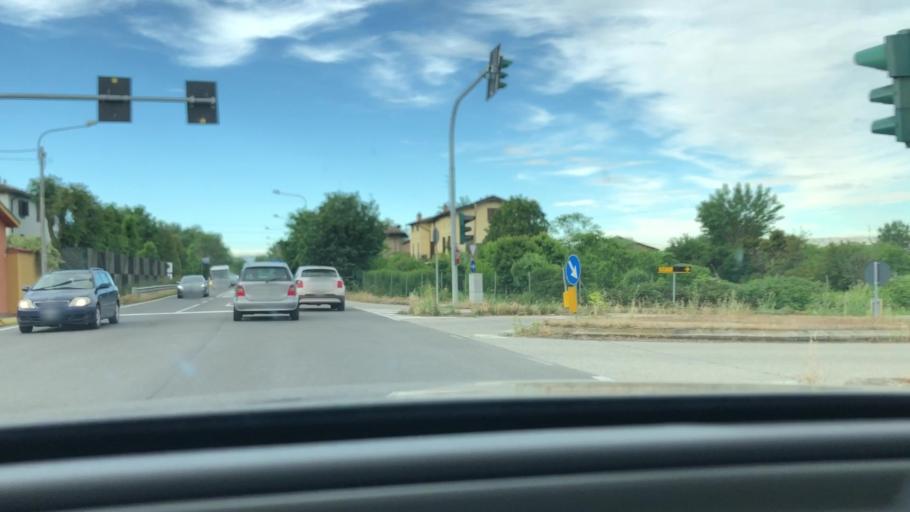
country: IT
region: Emilia-Romagna
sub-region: Provincia di Modena
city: San Damaso
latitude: 44.6039
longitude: 10.9321
